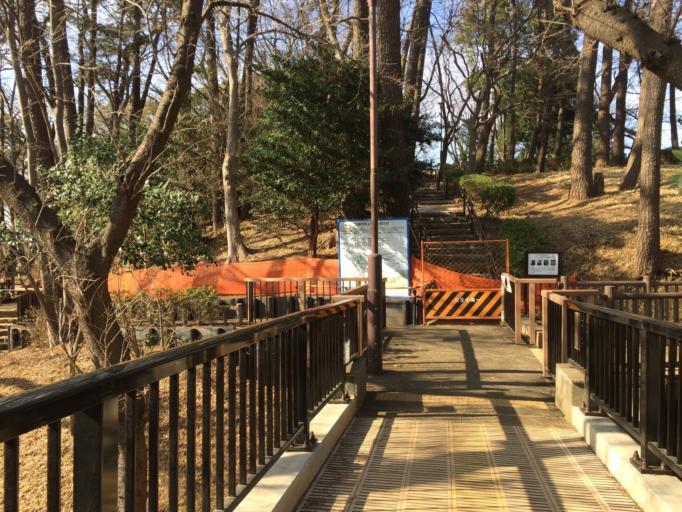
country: JP
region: Kanagawa
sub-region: Kawasaki-shi
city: Kawasaki
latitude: 35.5914
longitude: 139.6649
